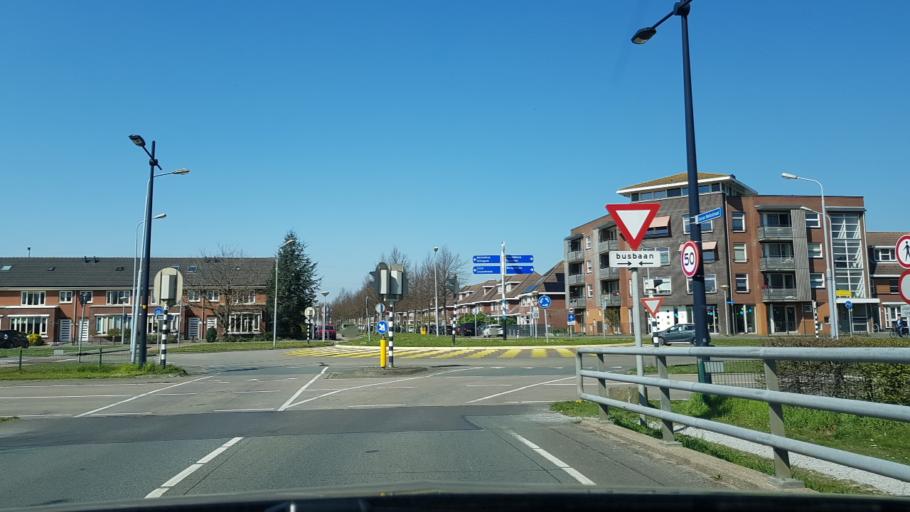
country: NL
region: South Holland
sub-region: Gemeente Hillegom
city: Hillegom
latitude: 52.2740
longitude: 4.6273
